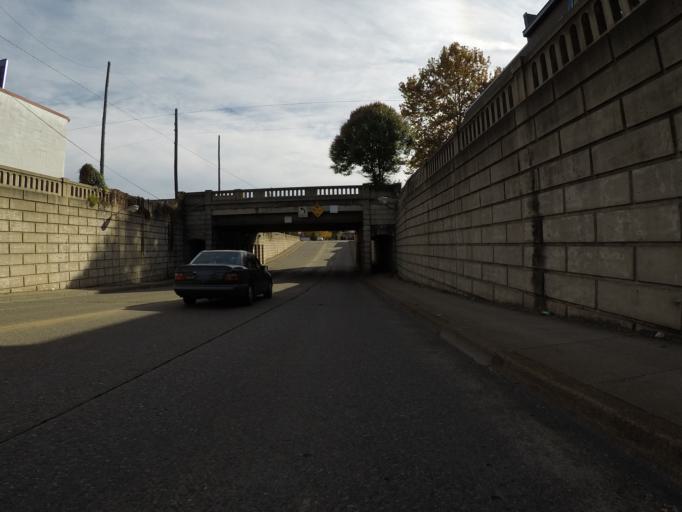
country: US
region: West Virginia
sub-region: Cabell County
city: Huntington
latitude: 38.4138
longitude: -82.4563
